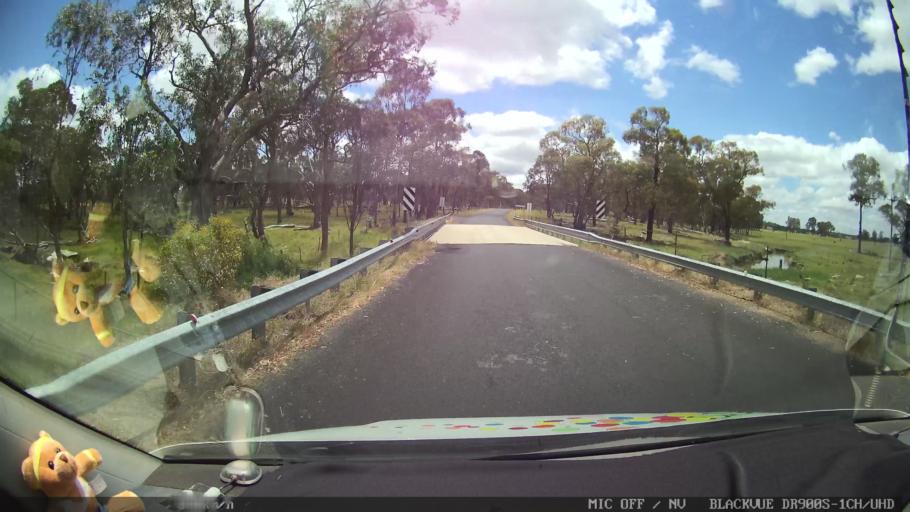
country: AU
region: New South Wales
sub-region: Glen Innes Severn
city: Glen Innes
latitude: -29.4199
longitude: 151.7296
